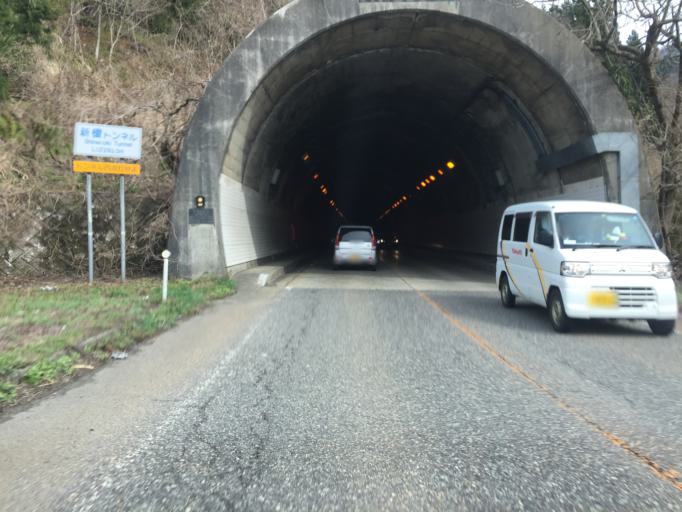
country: JP
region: Niigata
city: Nagaoka
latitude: 37.4556
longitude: 138.9232
